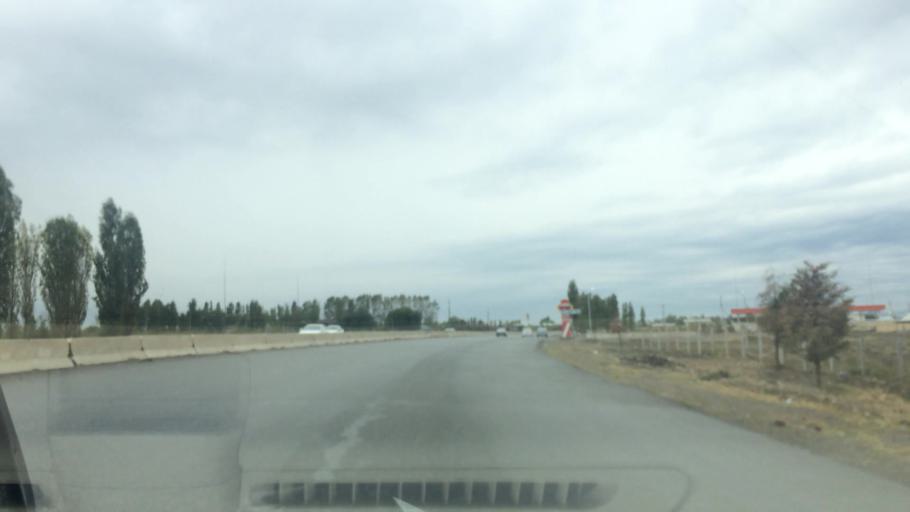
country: UZ
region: Jizzax
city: Jizzax
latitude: 40.0239
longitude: 67.6155
